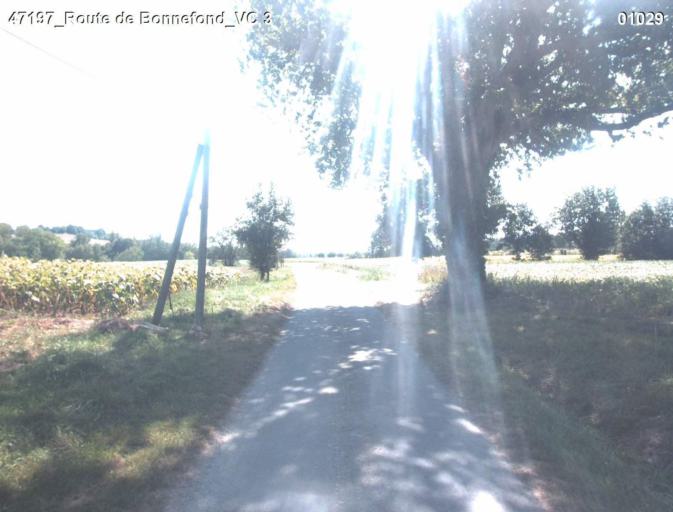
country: FR
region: Aquitaine
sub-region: Departement du Lot-et-Garonne
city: Laplume
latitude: 44.1044
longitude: 0.4753
